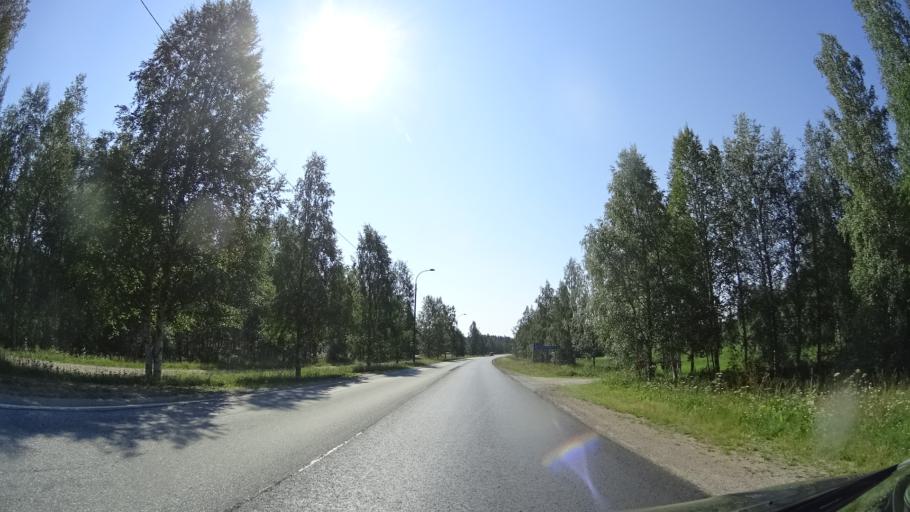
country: FI
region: North Karelia
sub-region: Joensuu
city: Juuka
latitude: 63.2424
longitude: 29.2770
